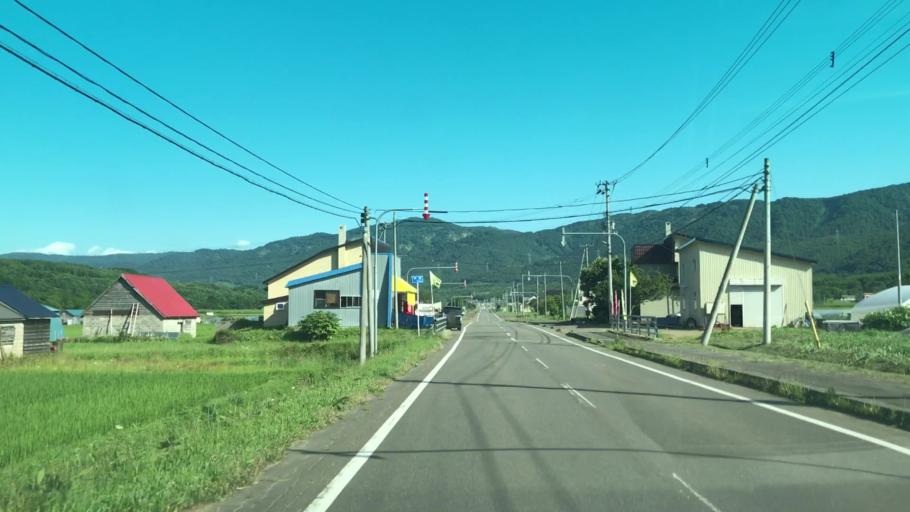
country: JP
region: Hokkaido
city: Yoichi
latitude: 43.0541
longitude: 140.7191
